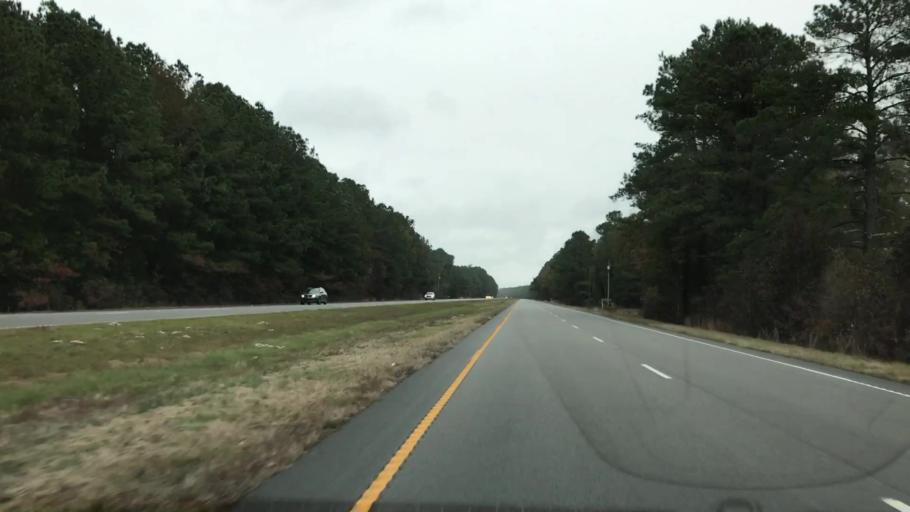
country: US
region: South Carolina
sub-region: Charleston County
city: Awendaw
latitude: 33.1135
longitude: -79.4582
